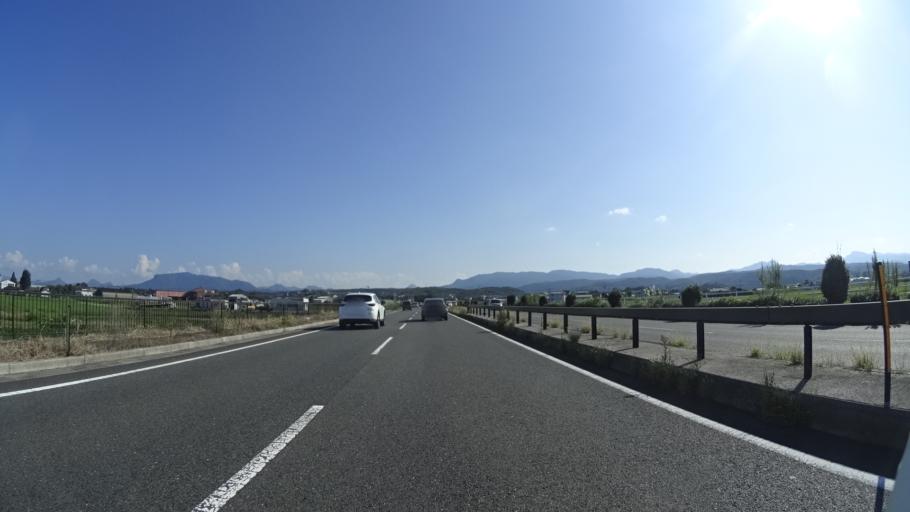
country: JP
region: Fukuoka
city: Yoshitomi
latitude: 33.5823
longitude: 131.1620
